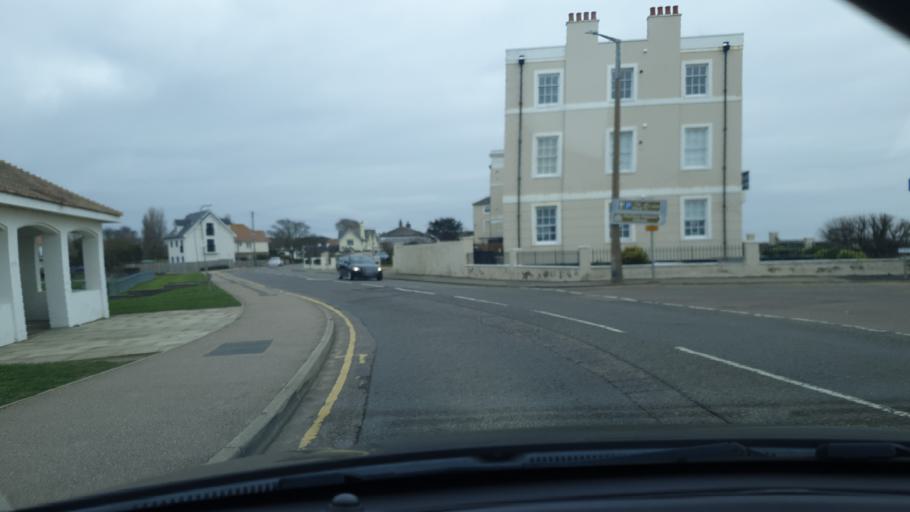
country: GB
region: England
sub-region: Essex
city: Walton-on-the-Naze
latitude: 51.8529
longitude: 1.2776
